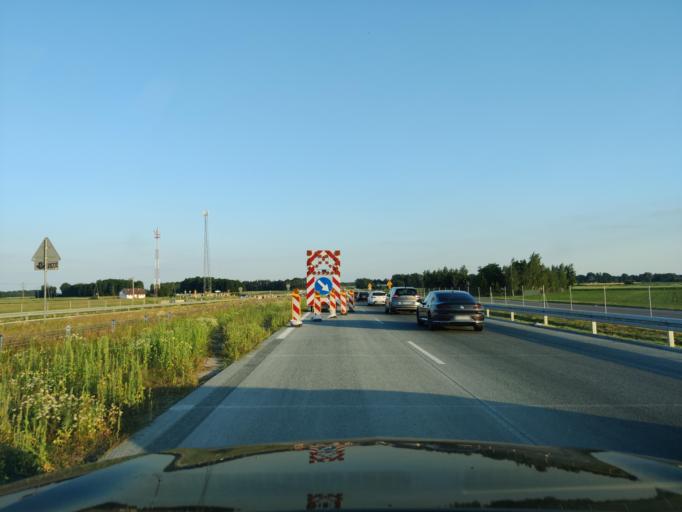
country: PL
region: Masovian Voivodeship
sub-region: Powiat plonski
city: Baboszewo
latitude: 52.7212
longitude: 20.3257
